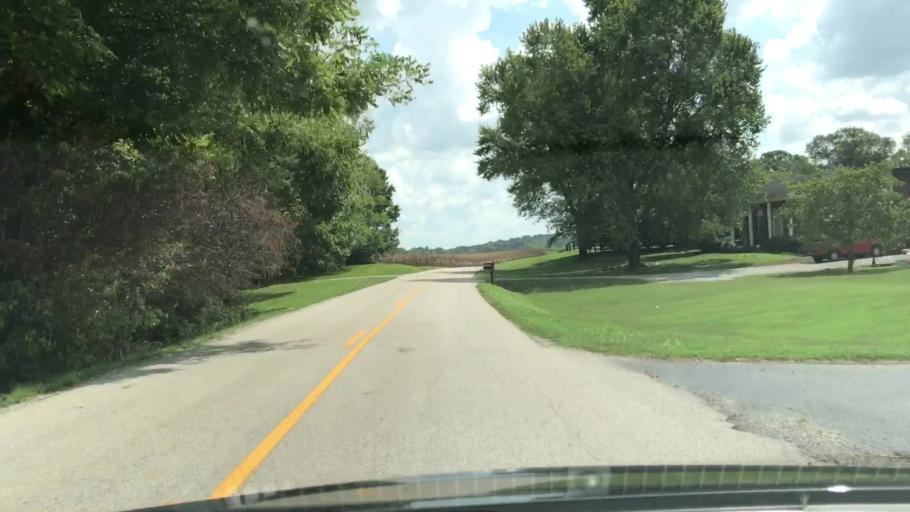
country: US
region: Kentucky
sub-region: Todd County
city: Guthrie
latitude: 36.7096
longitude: -87.0505
